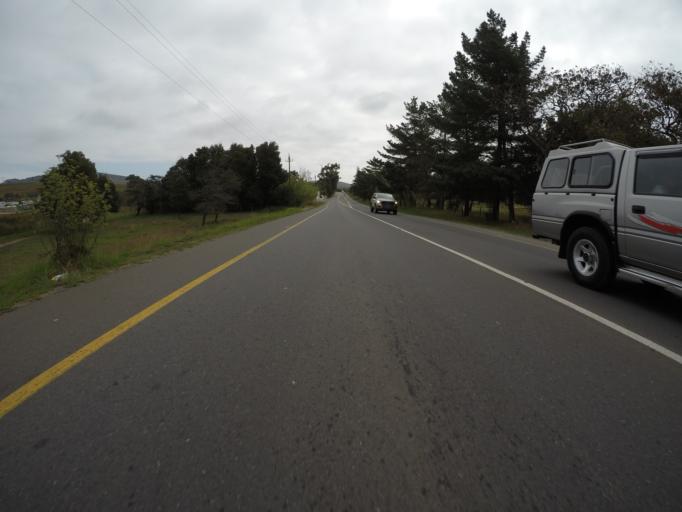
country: ZA
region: Western Cape
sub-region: City of Cape Town
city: Kraaifontein
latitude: -33.8413
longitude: 18.6123
